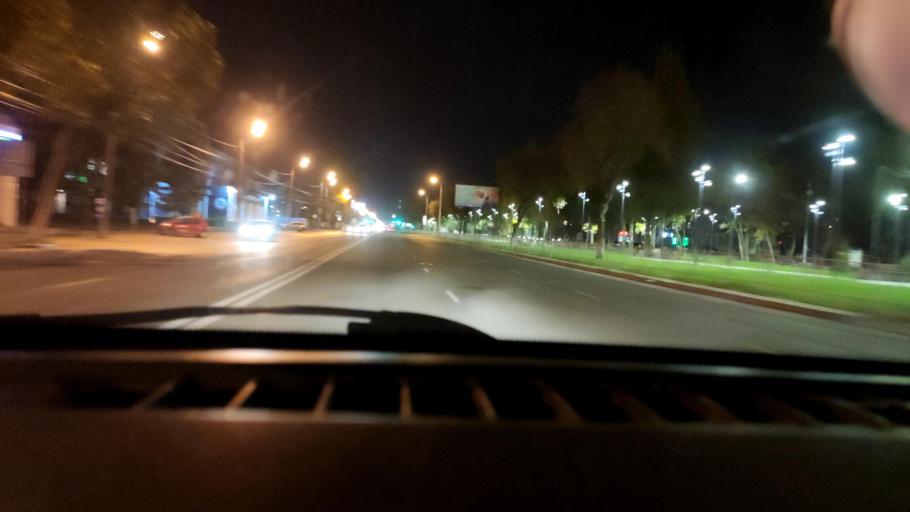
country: RU
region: Samara
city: Samara
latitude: 53.1930
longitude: 50.1908
